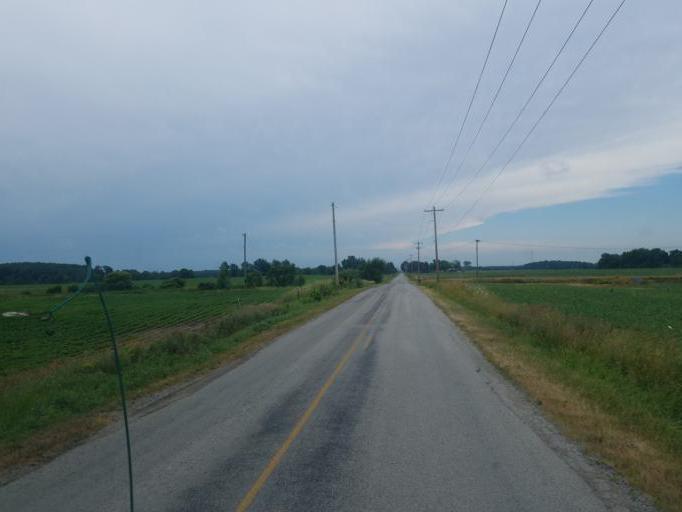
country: US
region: Indiana
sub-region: DeKalb County
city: Butler
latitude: 41.3796
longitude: -84.8888
